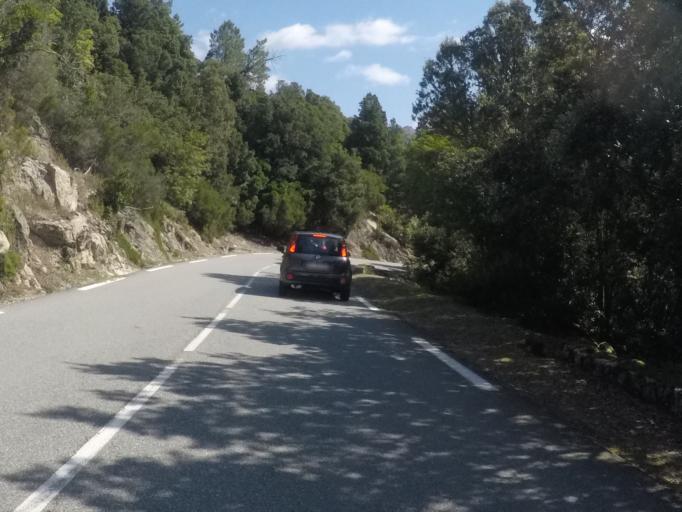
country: FR
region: Corsica
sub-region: Departement de la Corse-du-Sud
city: Zonza
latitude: 41.7672
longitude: 9.1698
